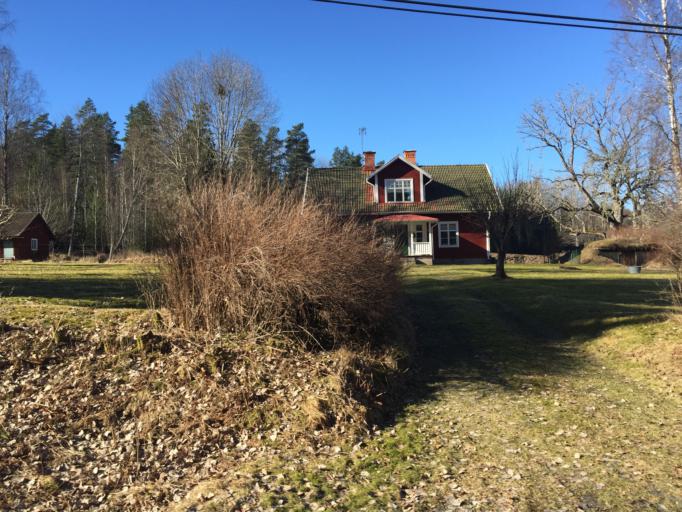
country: SE
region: Soedermanland
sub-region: Vingakers Kommun
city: Vingaker
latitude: 58.9482
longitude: 15.6665
